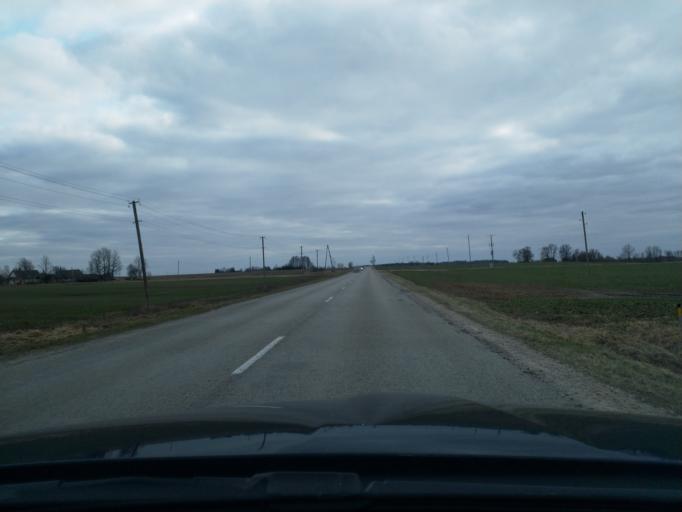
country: LV
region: Talsu Rajons
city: Sabile
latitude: 56.9573
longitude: 22.6123
